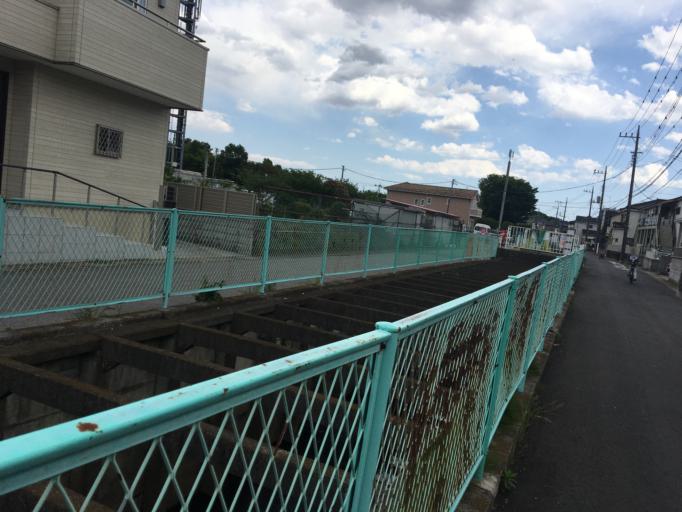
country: JP
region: Saitama
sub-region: Kawaguchi-shi
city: Hatogaya-honcho
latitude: 35.8371
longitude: 139.7569
